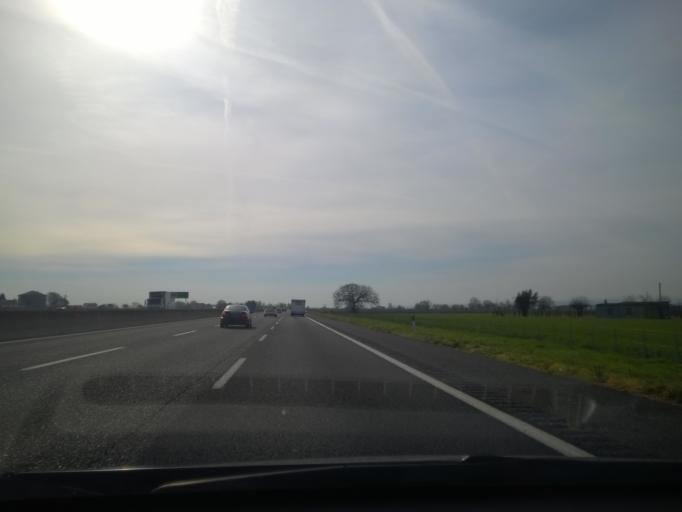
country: IT
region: Emilia-Romagna
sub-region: Forli-Cesena
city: Forlimpopoli
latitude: 44.2324
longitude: 12.1413
